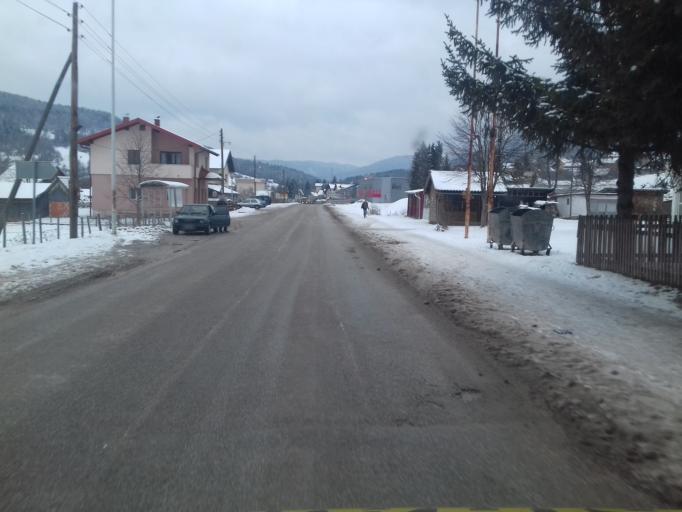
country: BA
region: Republika Srpska
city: Pale
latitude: 43.8822
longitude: 18.6083
